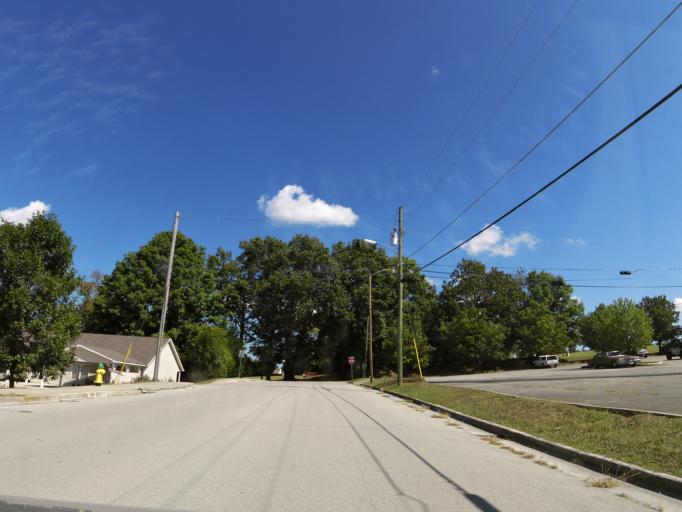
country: US
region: Tennessee
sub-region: Blount County
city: Maryville
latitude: 35.7615
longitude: -83.9712
